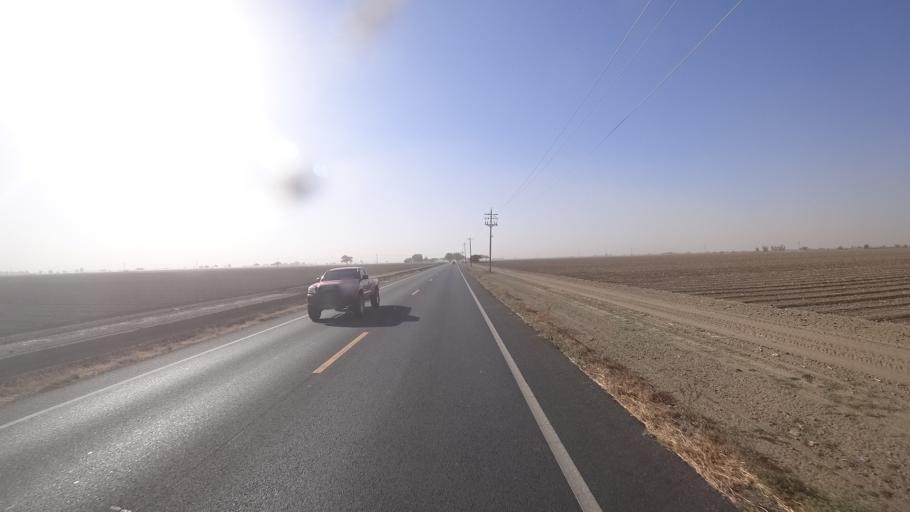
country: US
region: California
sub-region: Yolo County
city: Woodland
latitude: 38.7928
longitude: -121.7525
